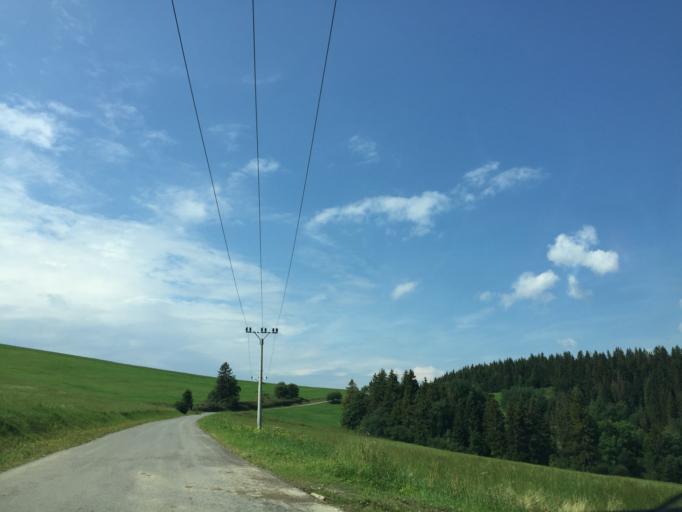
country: PL
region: Silesian Voivodeship
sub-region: Powiat zywiecki
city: Sopotnia Wielka
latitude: 49.4333
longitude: 19.3058
